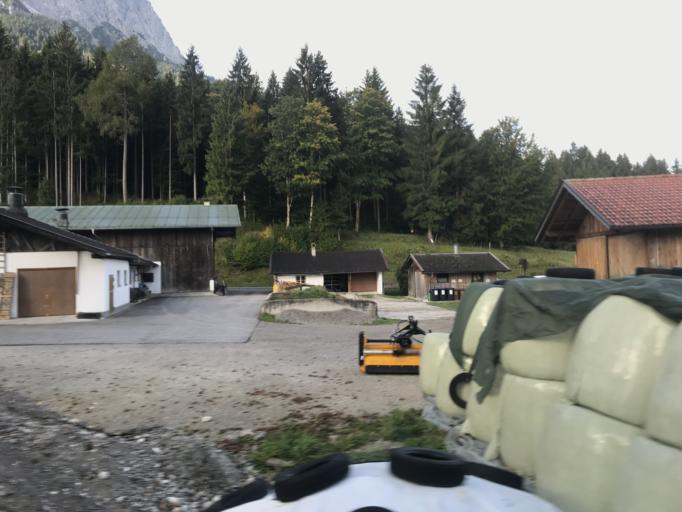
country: DE
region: Bavaria
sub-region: Upper Bavaria
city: Grainau
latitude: 47.4662
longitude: 11.0441
